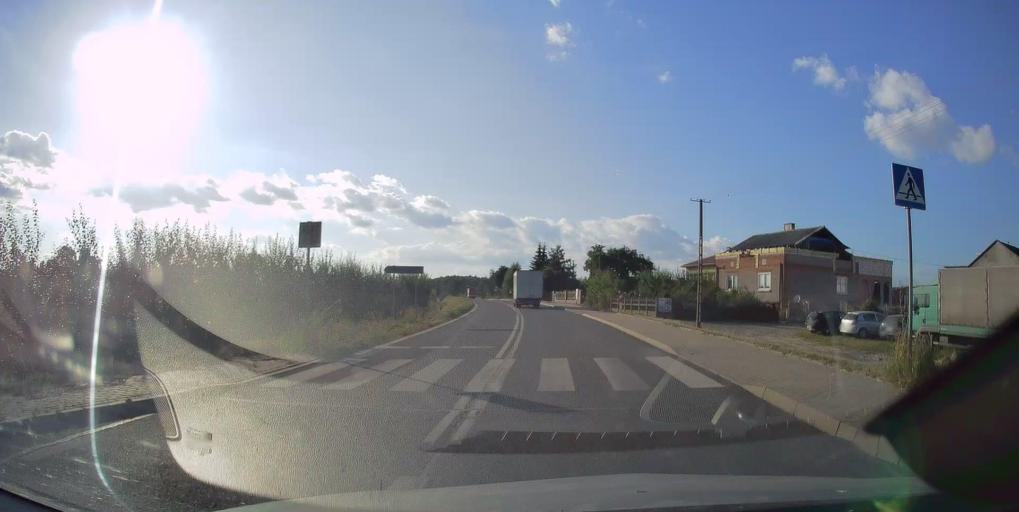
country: PL
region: Lodz Voivodeship
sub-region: Powiat rawski
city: Biala Rawska
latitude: 51.8054
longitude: 20.5012
